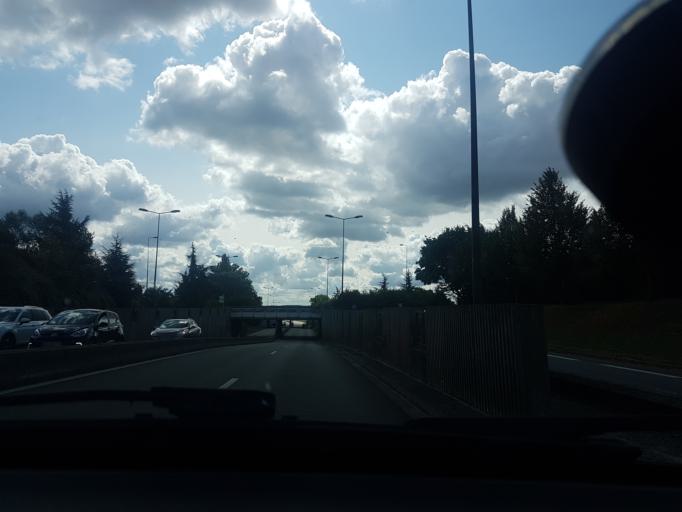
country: FR
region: Ile-de-France
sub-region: Departement des Yvelines
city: Noisy-le-Roi
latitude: 48.8449
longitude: 2.0557
